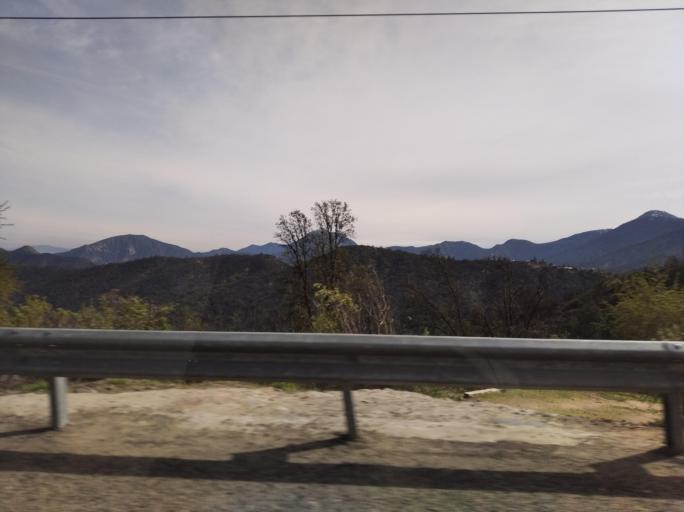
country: CL
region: Valparaiso
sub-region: Provincia de San Felipe
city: Llaillay
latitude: -33.0614
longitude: -71.0191
